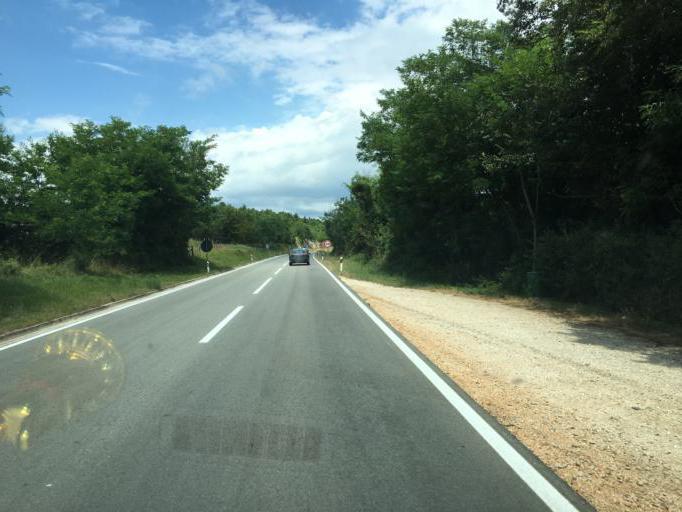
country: HR
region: Istarska
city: Karojba
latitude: 45.2277
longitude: 13.8402
